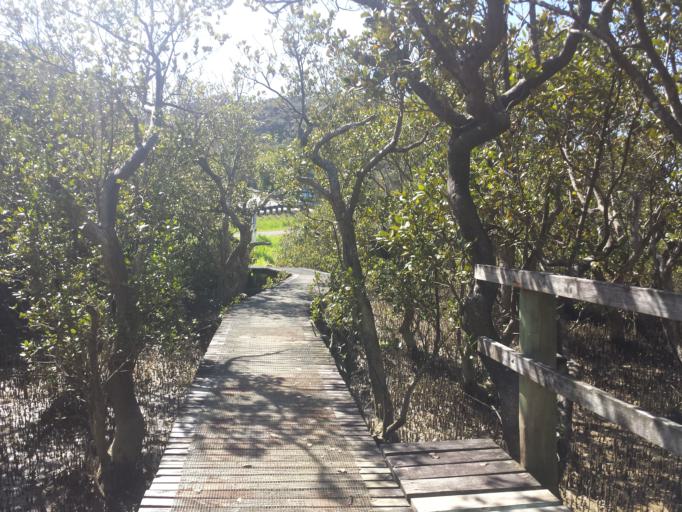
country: NZ
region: Northland
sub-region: Far North District
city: Paihia
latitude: -35.3043
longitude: 174.1017
